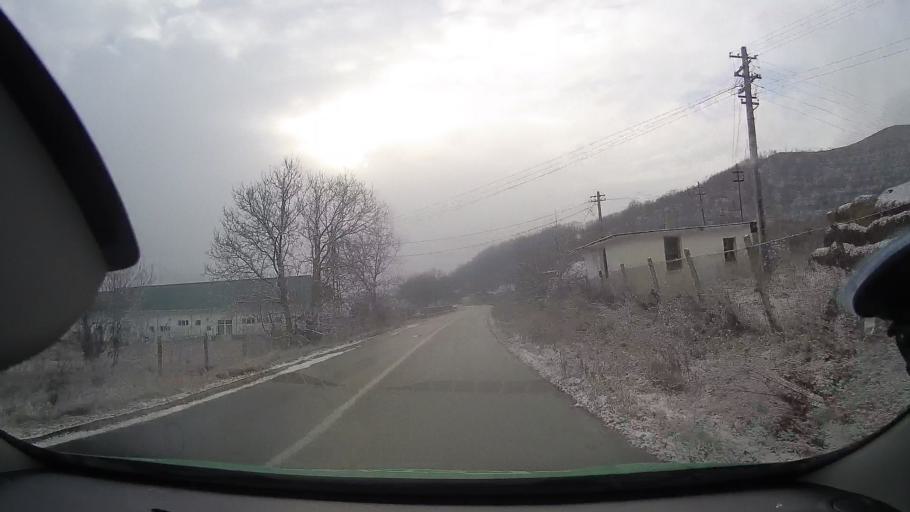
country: RO
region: Alba
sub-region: Comuna Rimetea
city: Rimetea
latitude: 46.4320
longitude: 23.5610
